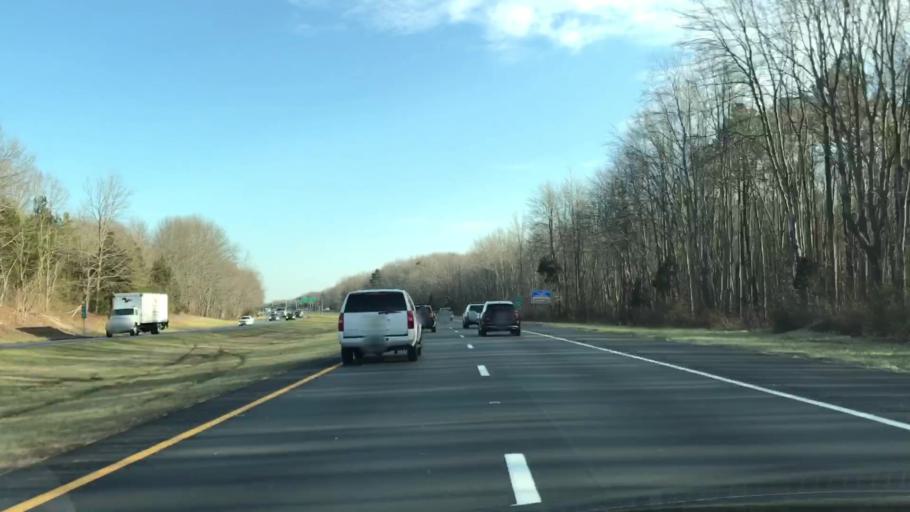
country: US
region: New Jersey
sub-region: Monmouth County
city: Shrewsbury
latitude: 40.1646
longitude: -74.4372
